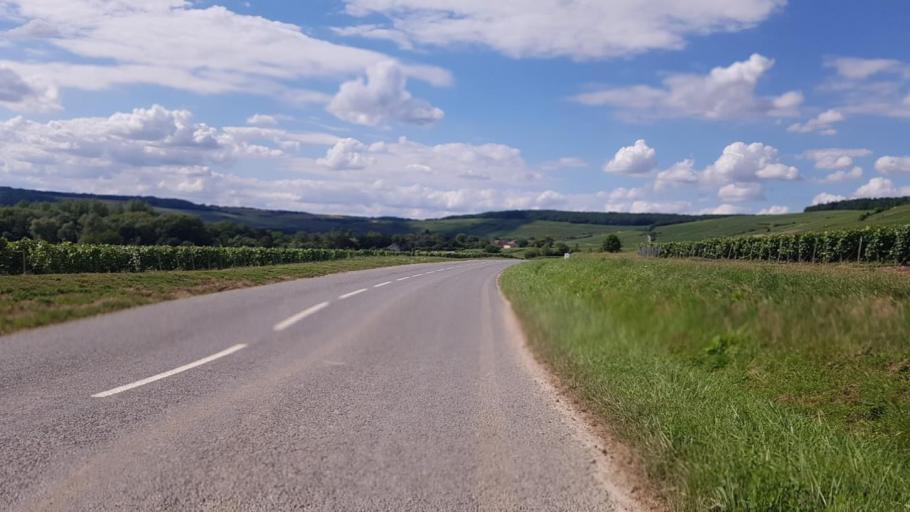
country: FR
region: Picardie
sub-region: Departement de l'Aisne
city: Crezancy
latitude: 49.0680
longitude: 3.5672
